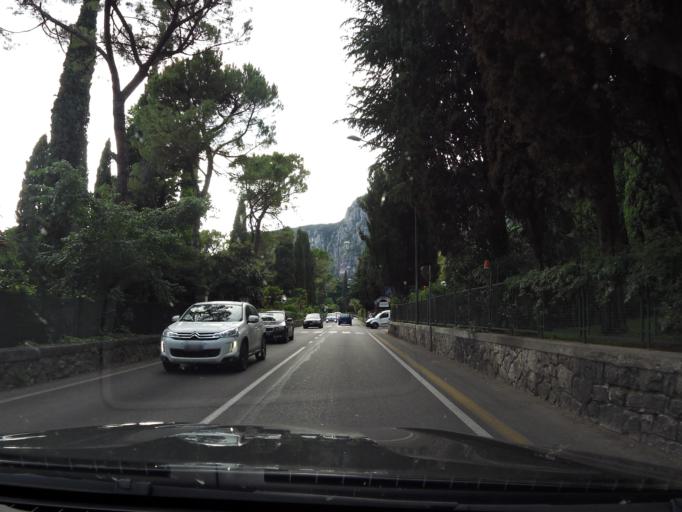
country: IT
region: Veneto
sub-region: Provincia di Verona
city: Garda
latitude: 45.5779
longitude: 10.6975
